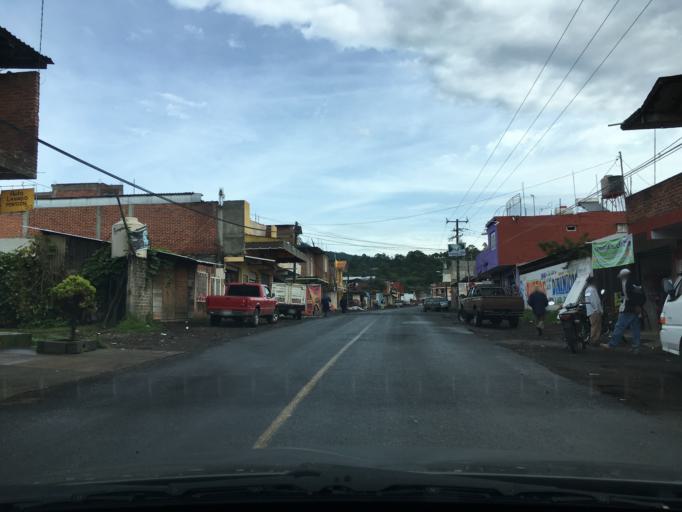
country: MX
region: Michoacan
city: Nuevo San Juan Parangaricutiro
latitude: 19.4227
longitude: -102.1342
